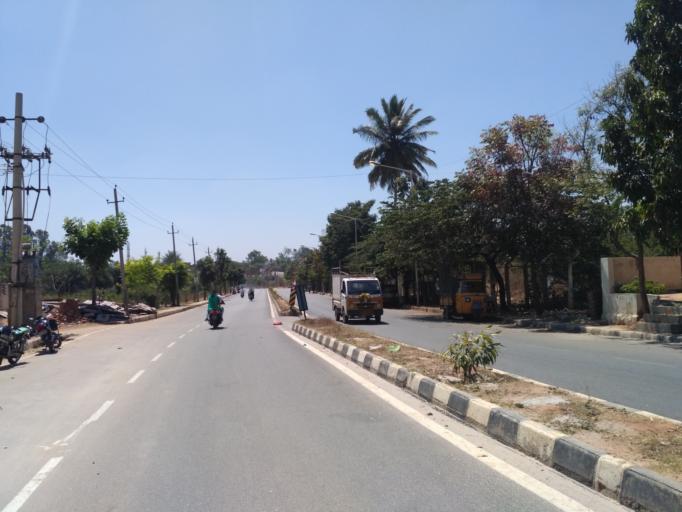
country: IN
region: Karnataka
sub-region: Bangalore Urban
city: Yelahanka
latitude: 13.0924
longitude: 77.5913
